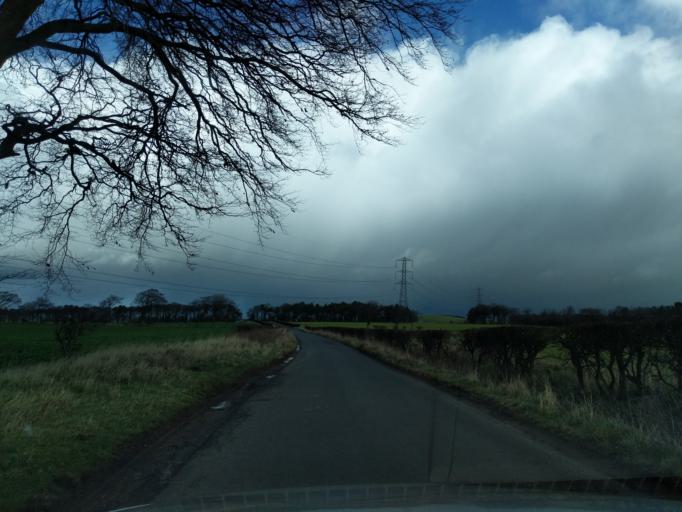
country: GB
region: Scotland
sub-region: Edinburgh
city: Currie
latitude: 55.8779
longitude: -3.3127
